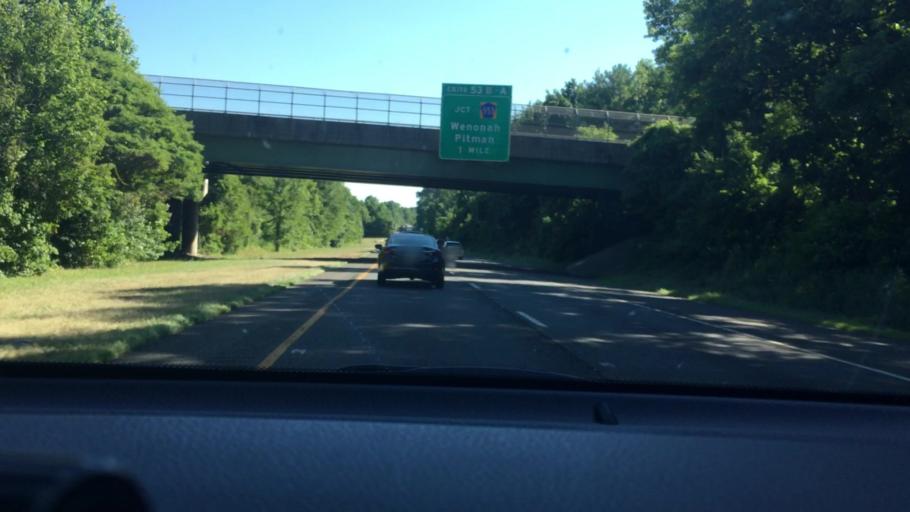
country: US
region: New Jersey
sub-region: Gloucester County
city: Pitman
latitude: 39.7691
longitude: -75.1188
